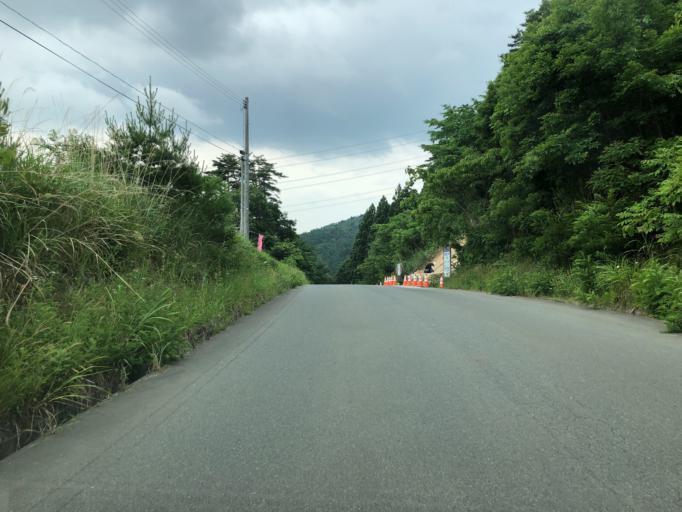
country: JP
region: Miyagi
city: Marumori
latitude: 37.8568
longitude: 140.8735
